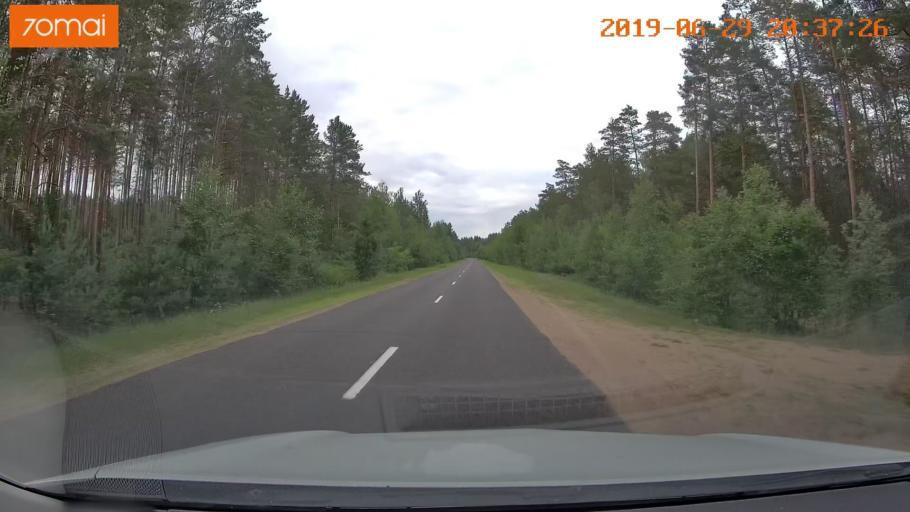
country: BY
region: Brest
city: Hantsavichy
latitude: 52.5380
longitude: 26.3644
